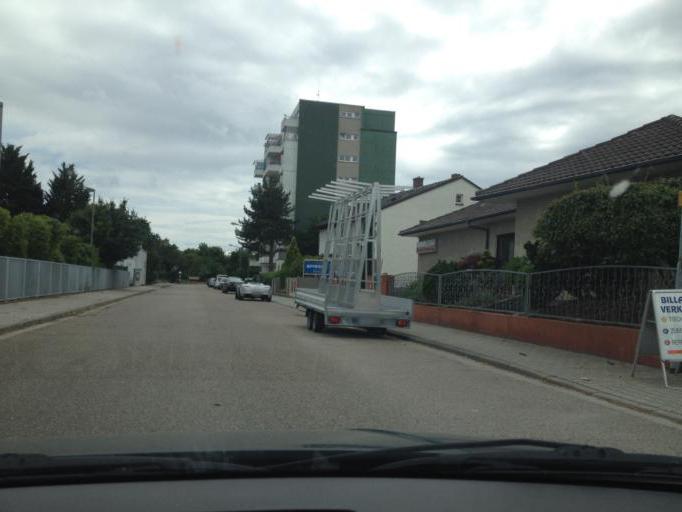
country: DE
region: Rheinland-Pfalz
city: Frankenthal
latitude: 49.5458
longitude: 8.3476
